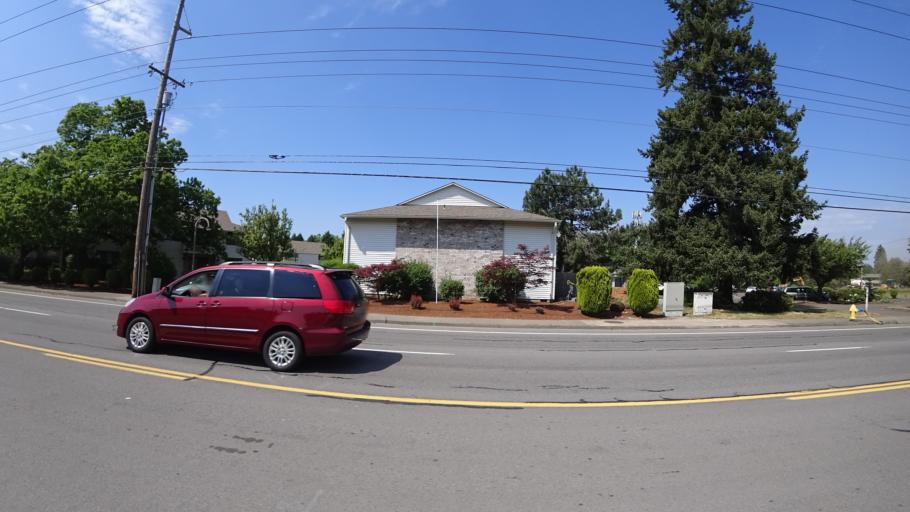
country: US
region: Oregon
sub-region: Multnomah County
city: Fairview
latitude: 45.5343
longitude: -122.4943
